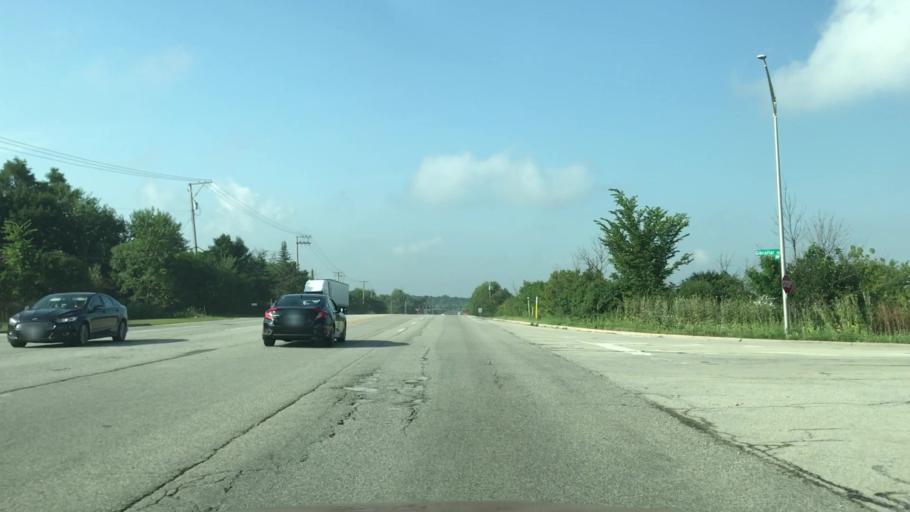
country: US
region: Illinois
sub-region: Will County
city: Bolingbrook
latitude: 41.6847
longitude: -88.0503
